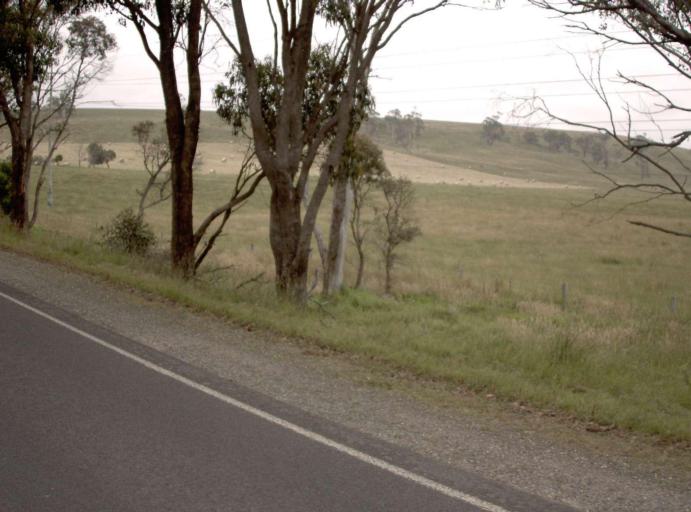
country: AU
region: Victoria
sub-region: Latrobe
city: Traralgon
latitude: -38.2494
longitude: 146.5325
